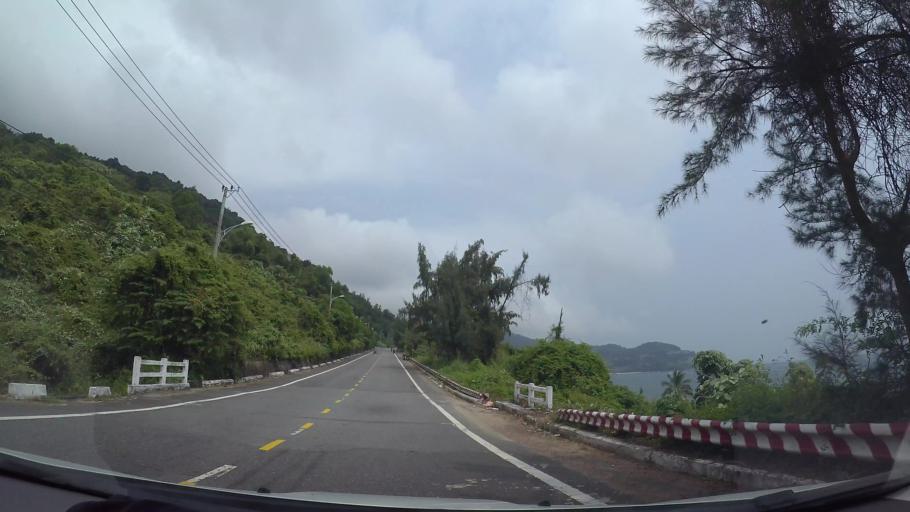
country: VN
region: Da Nang
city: Son Tra
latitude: 16.1039
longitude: 108.2852
